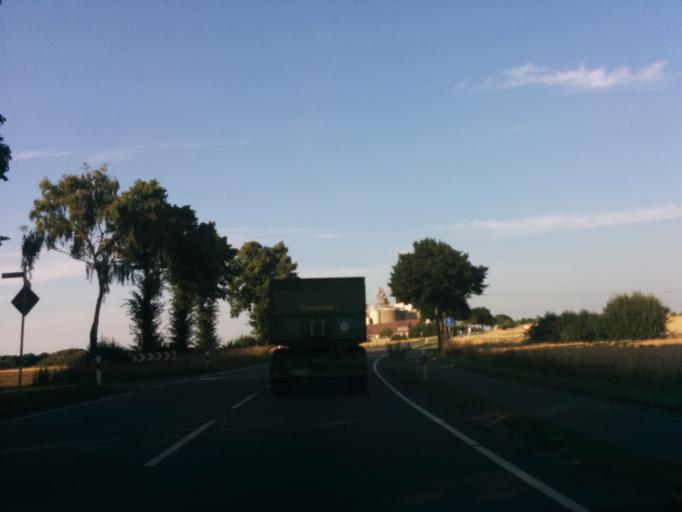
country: DE
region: North Rhine-Westphalia
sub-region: Regierungsbezirk Munster
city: Neuenkirchen
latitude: 52.2615
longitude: 7.3923
